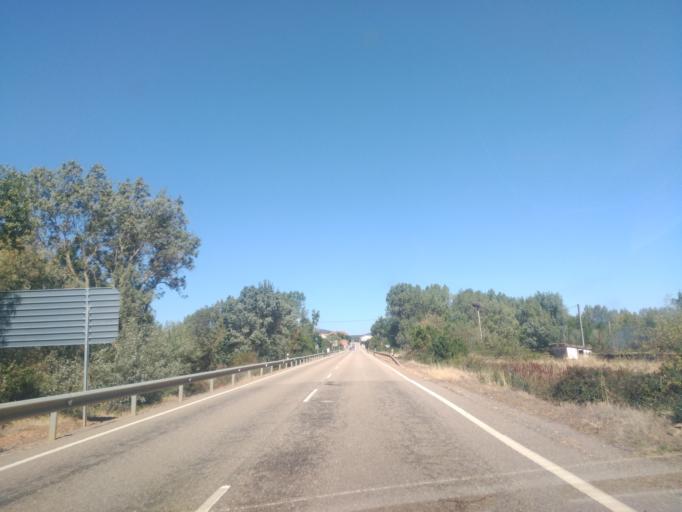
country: ES
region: Castille and Leon
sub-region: Provincia de Zamora
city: Tabara
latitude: 41.8229
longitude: -5.9530
